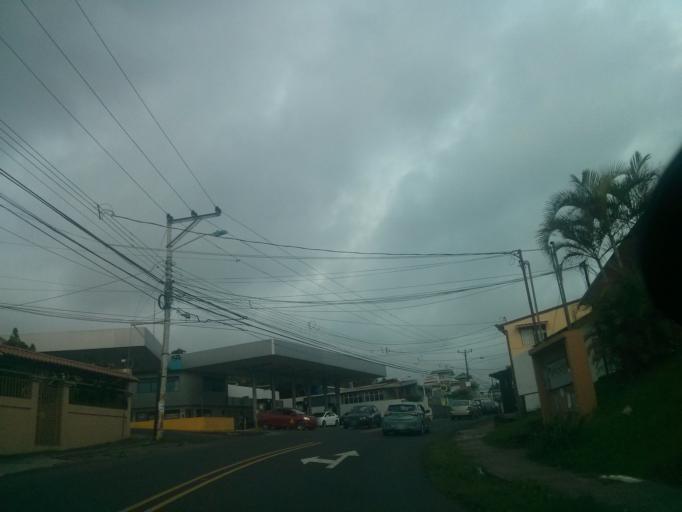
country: CR
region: Heredia
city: San Pablo
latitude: 9.9931
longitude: -84.1057
